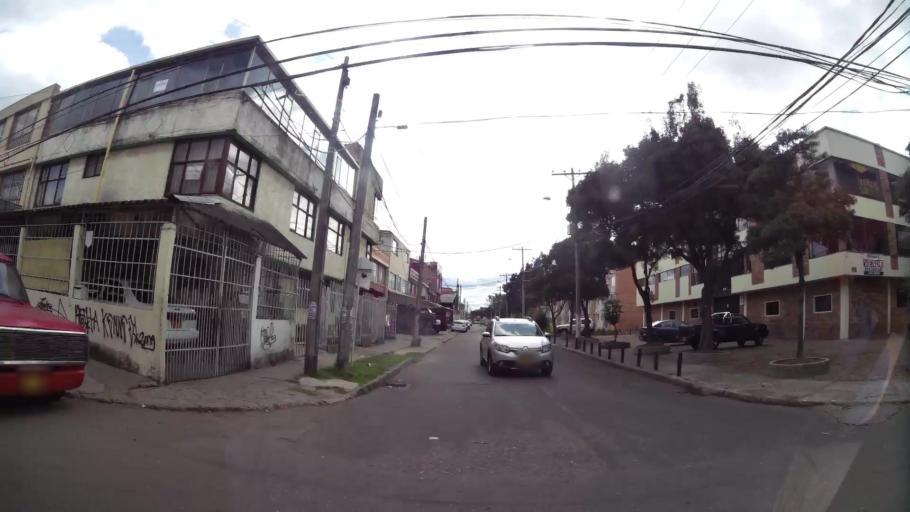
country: CO
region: Bogota D.C.
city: Bogota
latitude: 4.6131
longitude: -74.1387
